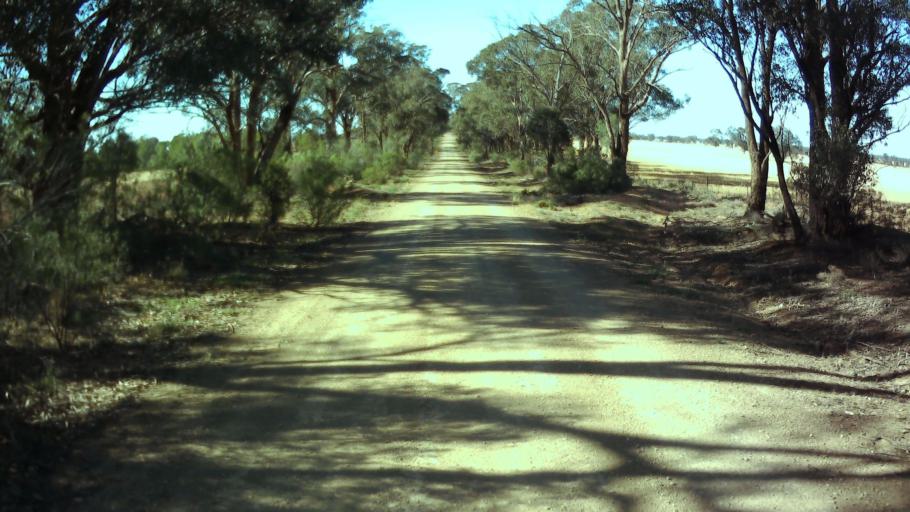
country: AU
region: New South Wales
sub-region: Weddin
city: Grenfell
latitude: -33.9028
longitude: 147.8782
